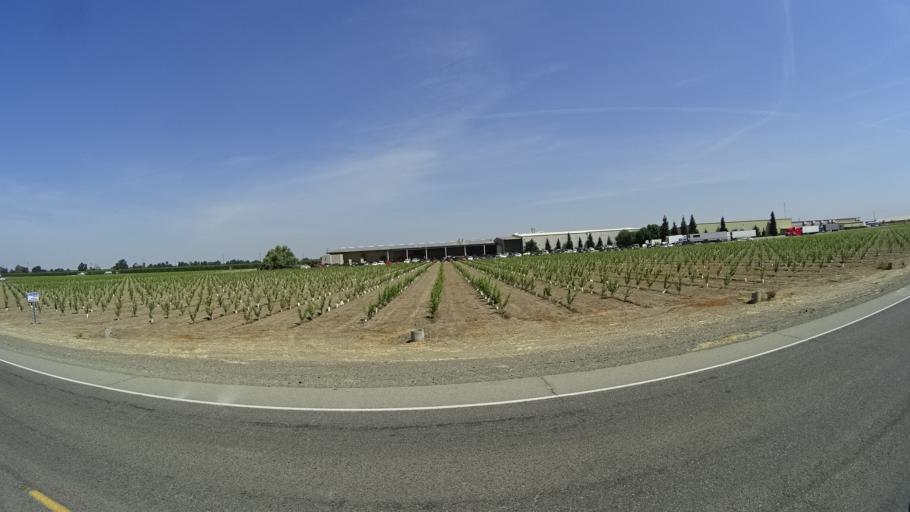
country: US
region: California
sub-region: Fresno County
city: Laton
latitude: 36.4009
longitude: -119.7419
